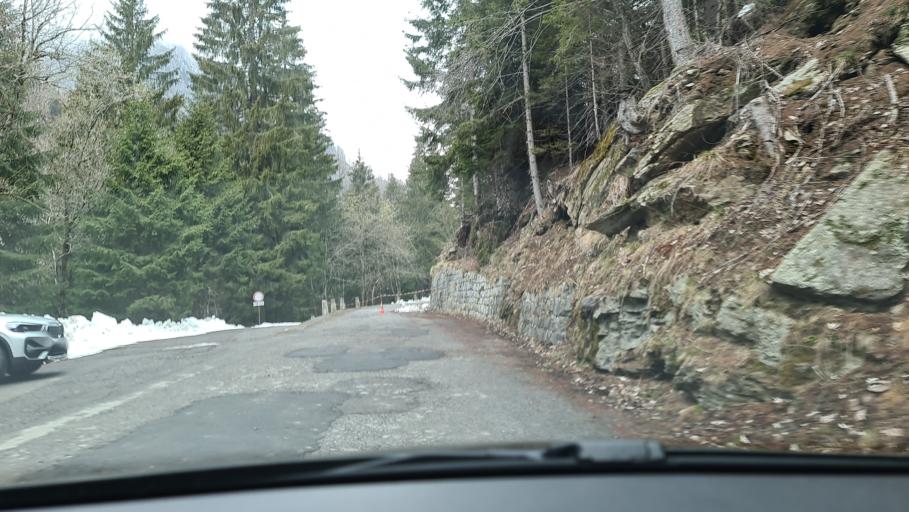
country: CH
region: Ticino
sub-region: Leventina District
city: Airolo
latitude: 46.4482
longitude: 8.6627
